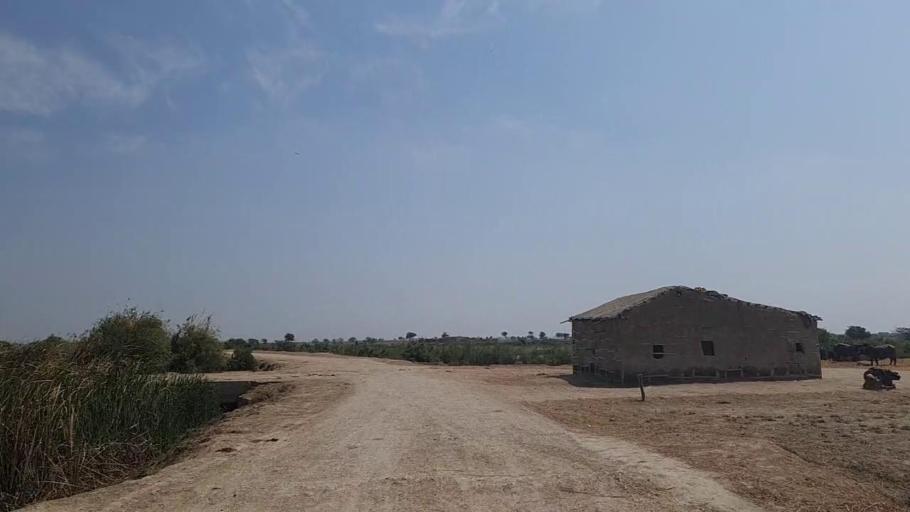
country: PK
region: Sindh
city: Mirpur Batoro
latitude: 24.5848
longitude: 68.2966
